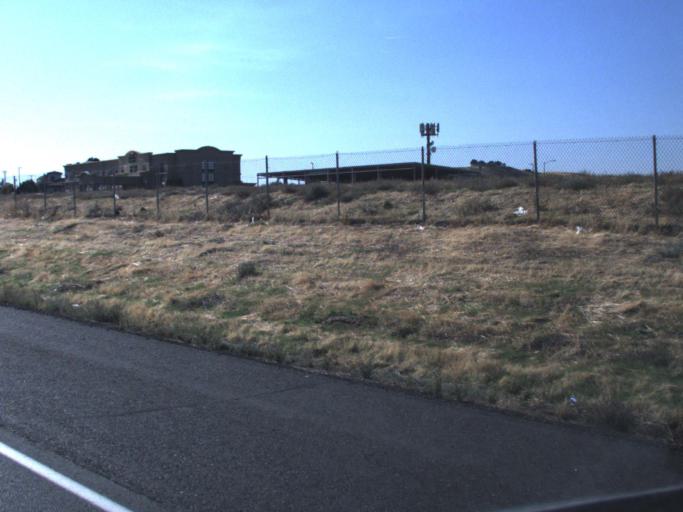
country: US
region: Washington
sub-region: Benton County
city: Kennewick
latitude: 46.1871
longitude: -119.1736
